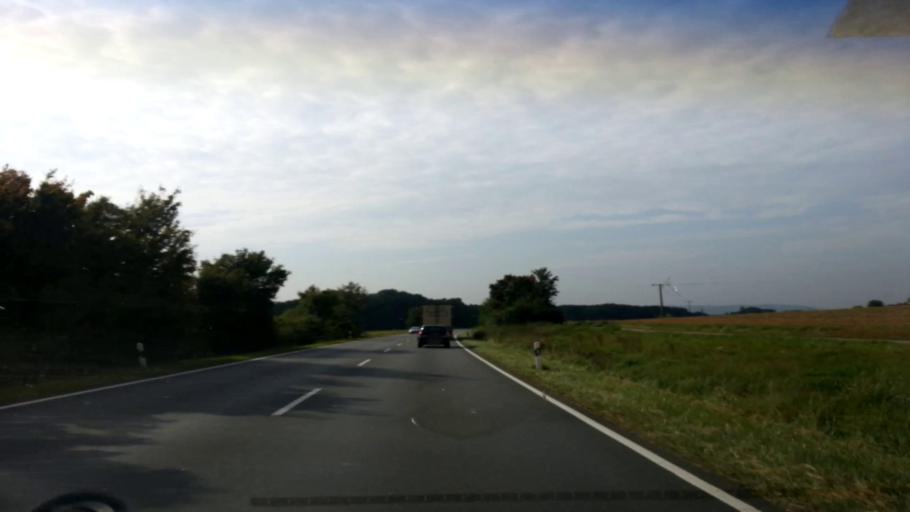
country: DE
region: Bavaria
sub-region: Regierungsbezirk Unterfranken
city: Prichsenstadt
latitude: 49.8065
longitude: 10.3609
